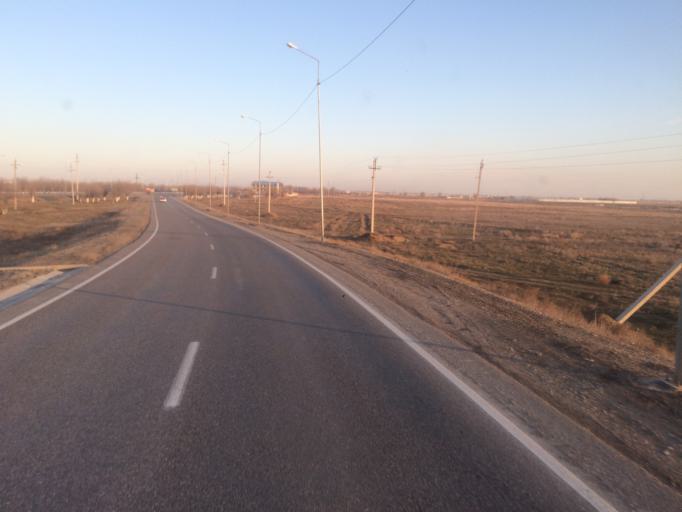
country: KZ
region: Ongtustik Qazaqstan
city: Turkestan
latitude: 43.2736
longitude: 68.3375
